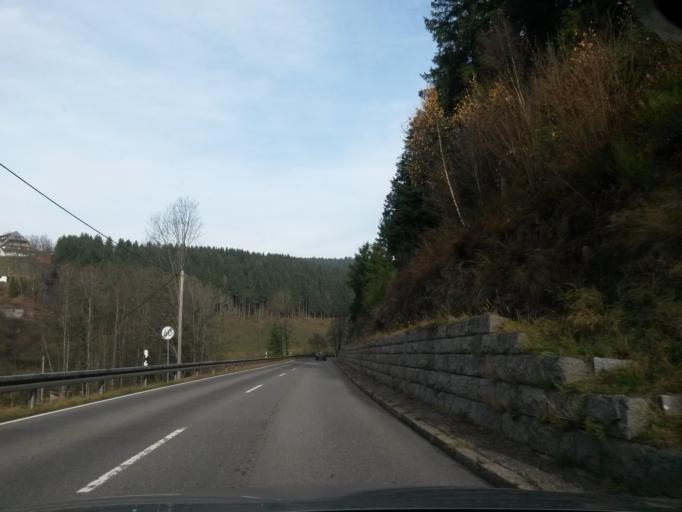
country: DE
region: Baden-Wuerttemberg
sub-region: Freiburg Region
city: Tennenbronn
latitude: 48.1701
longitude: 8.3260
